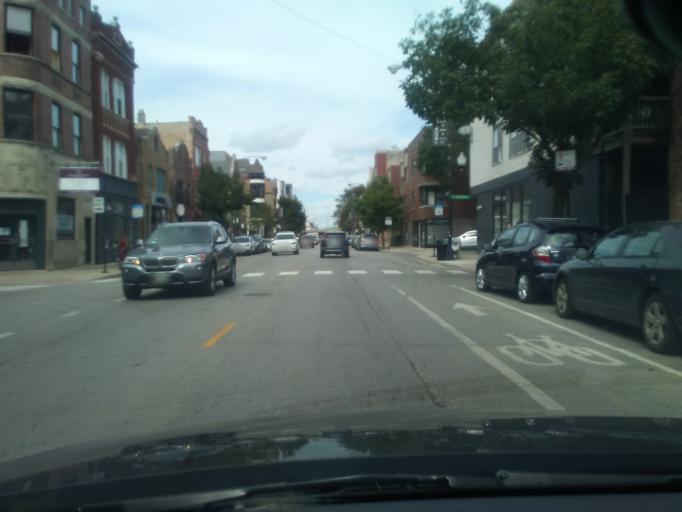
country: US
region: Illinois
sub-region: Cook County
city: Chicago
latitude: 41.9192
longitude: -87.6776
